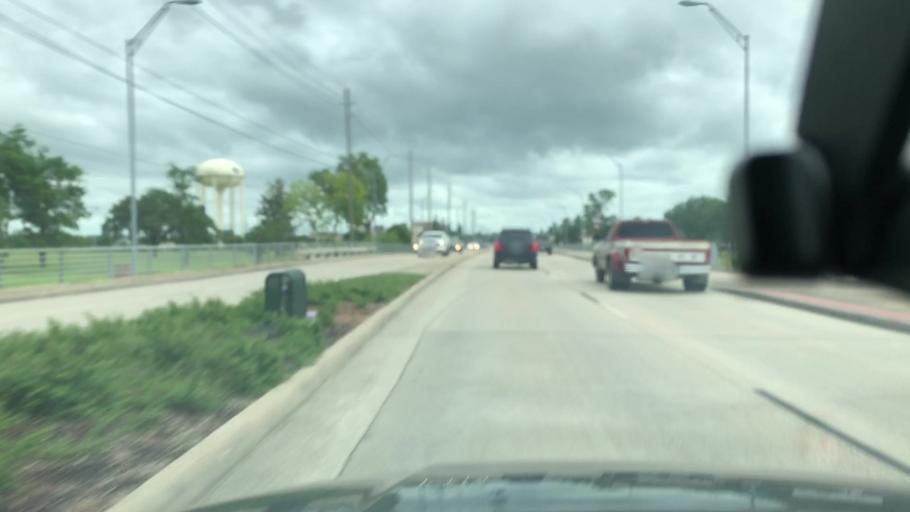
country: US
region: Texas
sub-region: Brazoria County
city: Brookside Village
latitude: 29.5668
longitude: -95.3507
